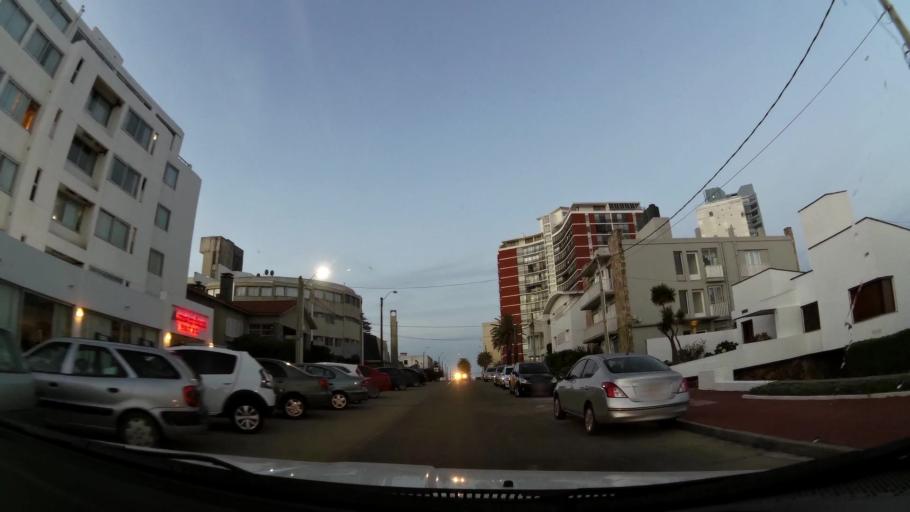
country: UY
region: Maldonado
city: Punta del Este
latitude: -34.9677
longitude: -54.9485
